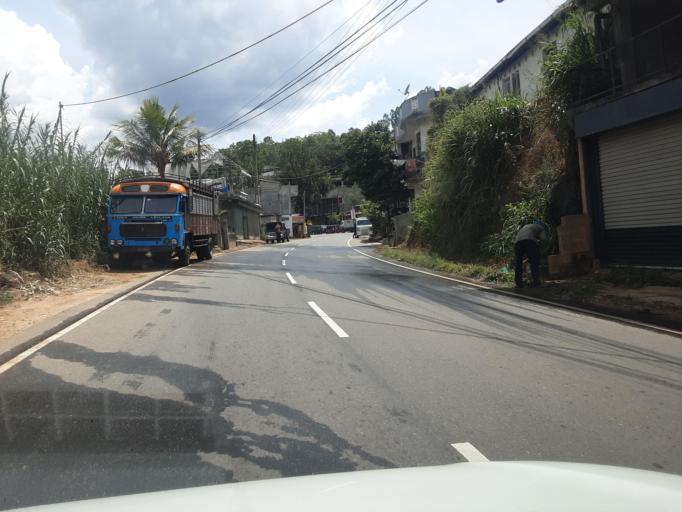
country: LK
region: Central
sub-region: Nuwara Eliya District
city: Nuwara Eliya
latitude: 6.9211
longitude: 80.9006
